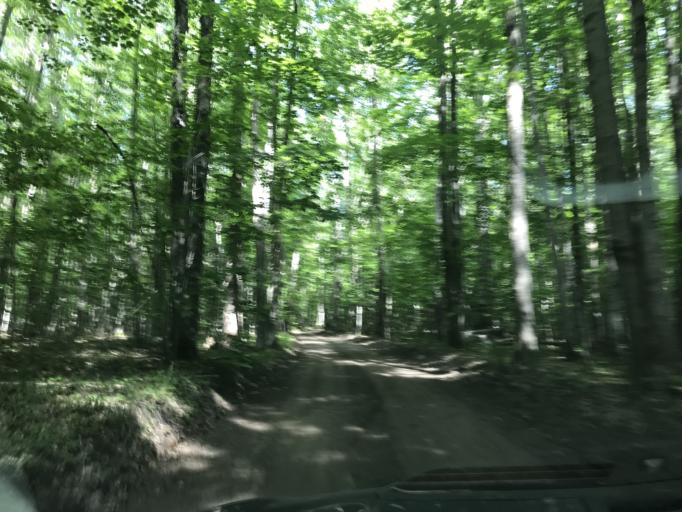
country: US
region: Michigan
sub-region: Cheboygan County
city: Indian River
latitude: 45.5928
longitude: -84.6838
